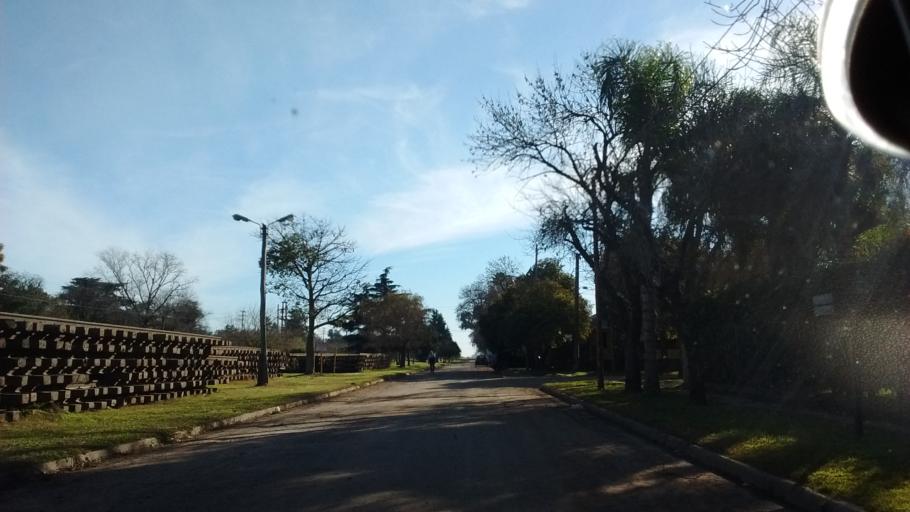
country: AR
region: Santa Fe
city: Funes
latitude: -32.9159
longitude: -60.8156
